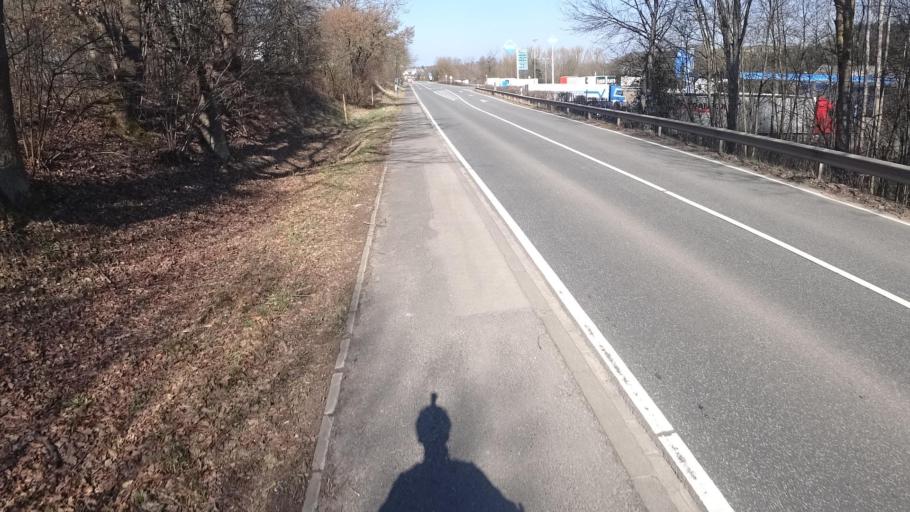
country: DE
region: Rheinland-Pfalz
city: Dichtelbach
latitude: 49.9954
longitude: 7.6838
